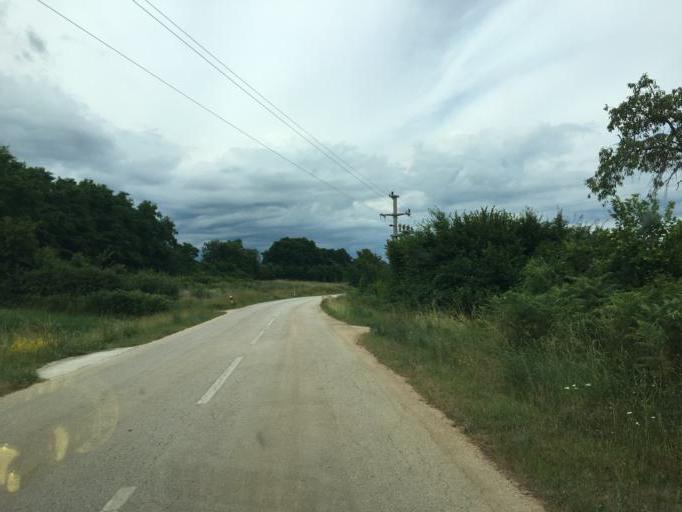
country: HR
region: Istarska
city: Pazin
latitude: 45.2286
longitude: 13.9111
